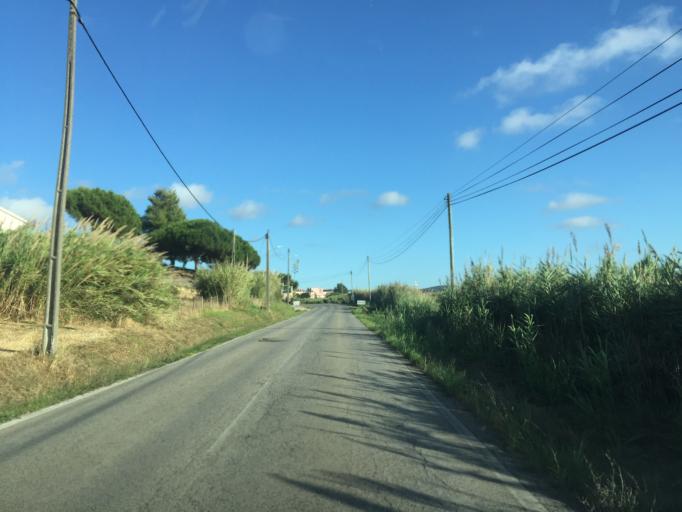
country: PT
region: Lisbon
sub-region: Torres Vedras
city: A dos Cunhados
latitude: 39.1589
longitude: -9.3031
